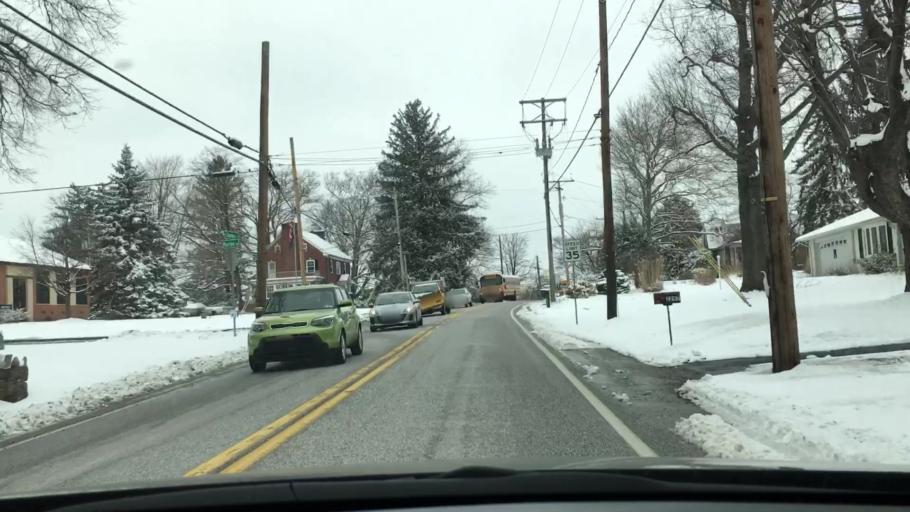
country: US
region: Pennsylvania
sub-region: York County
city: East York
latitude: 39.9968
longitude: -76.7066
